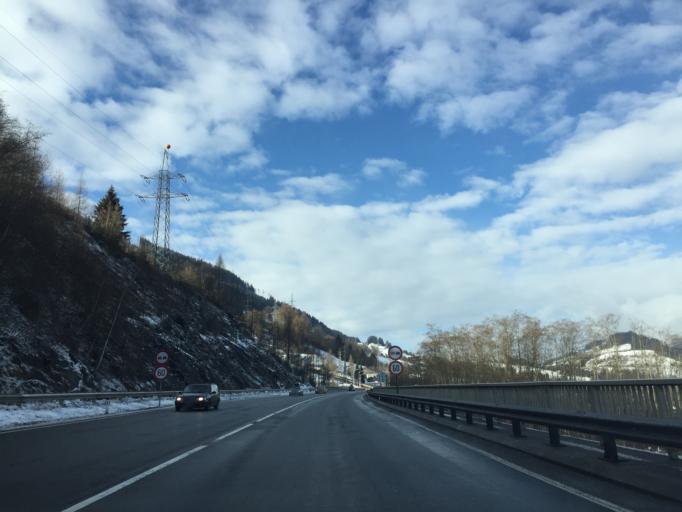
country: AT
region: Salzburg
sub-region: Politischer Bezirk Zell am See
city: Lend
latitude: 47.2948
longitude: 13.0614
